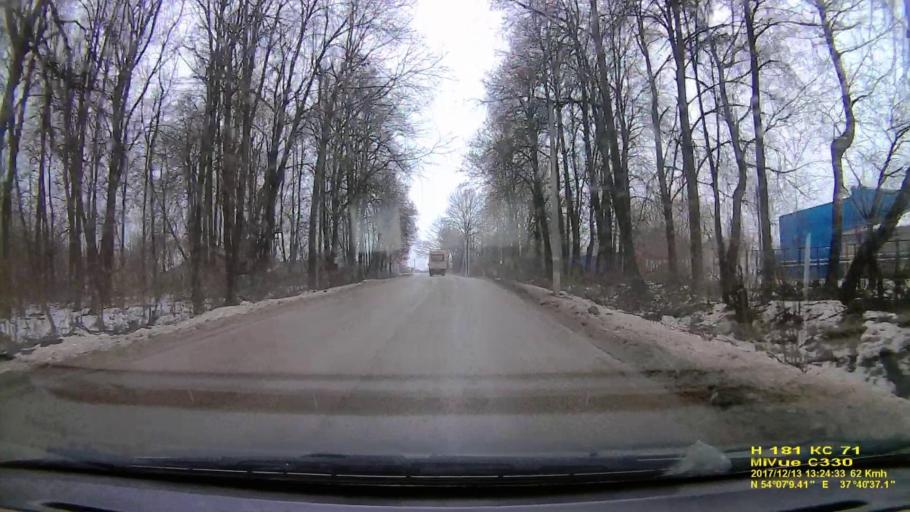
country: RU
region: Tula
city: Skuratovskiy
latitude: 54.1192
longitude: 37.6768
